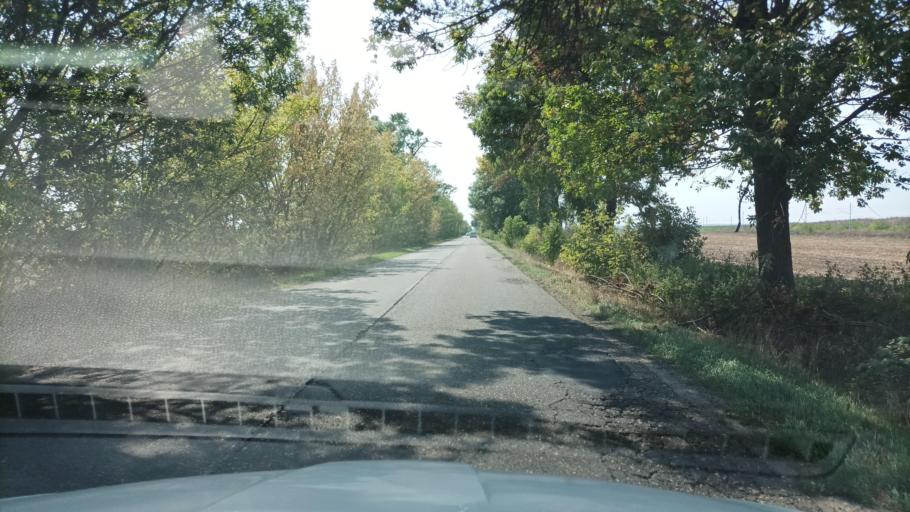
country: HU
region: Pest
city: Tura
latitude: 47.6336
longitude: 19.6320
